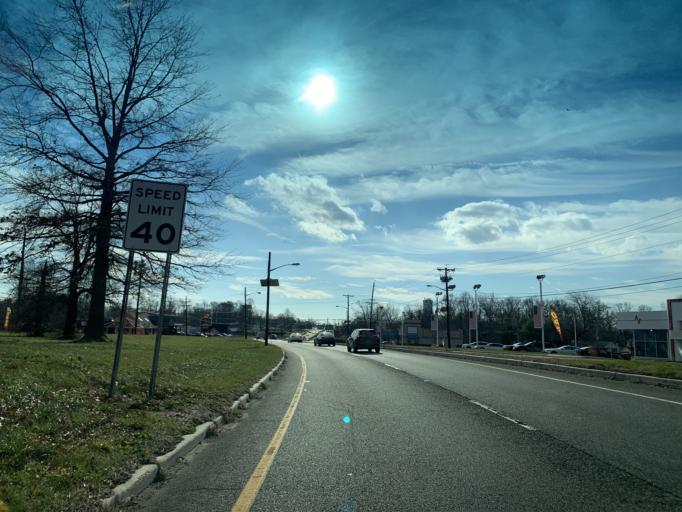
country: US
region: New Jersey
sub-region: Burlington County
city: Bordentown
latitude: 40.1517
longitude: -74.7002
